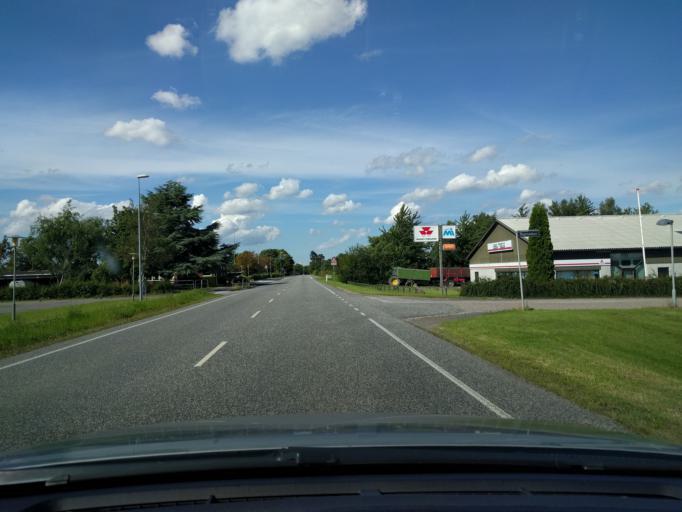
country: DK
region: Zealand
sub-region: Guldborgsund Kommune
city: Stubbekobing
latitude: 54.7993
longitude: 11.9930
